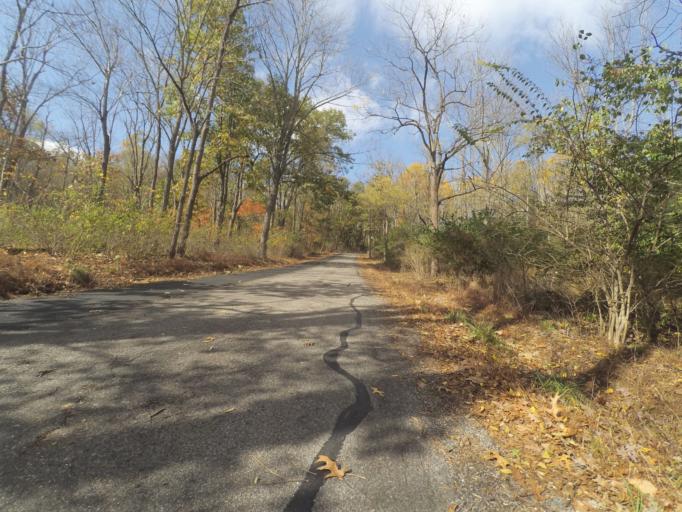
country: US
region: Pennsylvania
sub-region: Centre County
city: Stormstown
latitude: 40.8735
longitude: -77.9945
